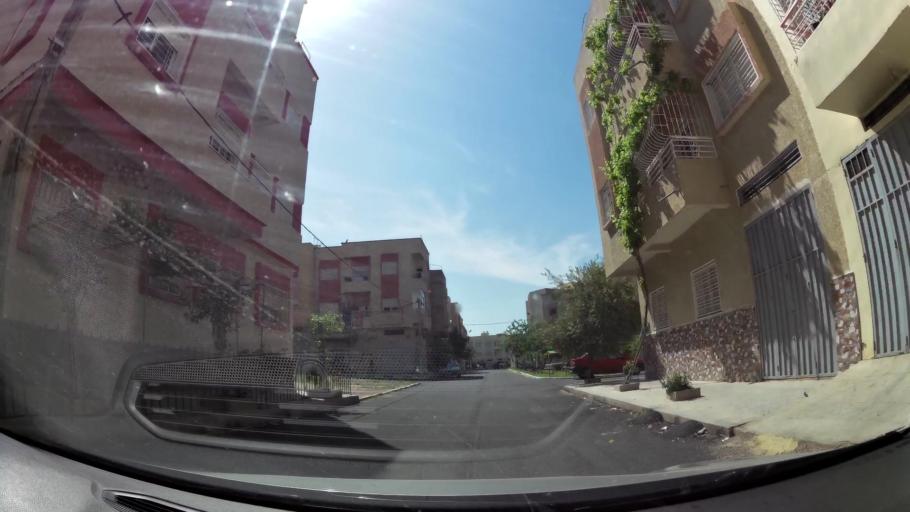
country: MA
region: Fes-Boulemane
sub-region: Fes
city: Fes
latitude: 34.0079
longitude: -5.0330
